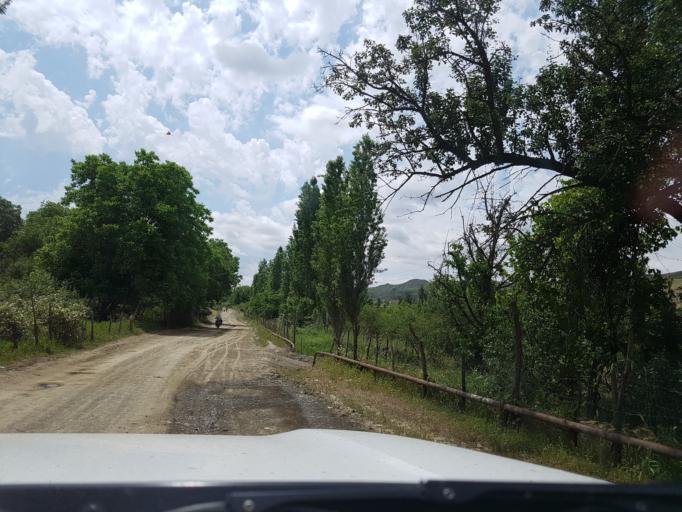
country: TM
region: Ahal
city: Baharly
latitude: 38.1972
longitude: 57.0041
